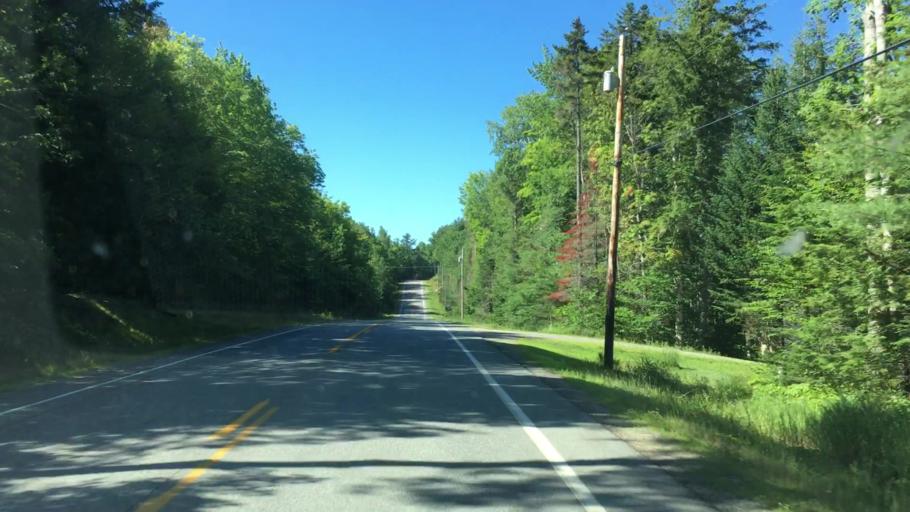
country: US
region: Maine
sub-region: Hancock County
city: Dedham
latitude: 44.6801
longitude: -68.6679
